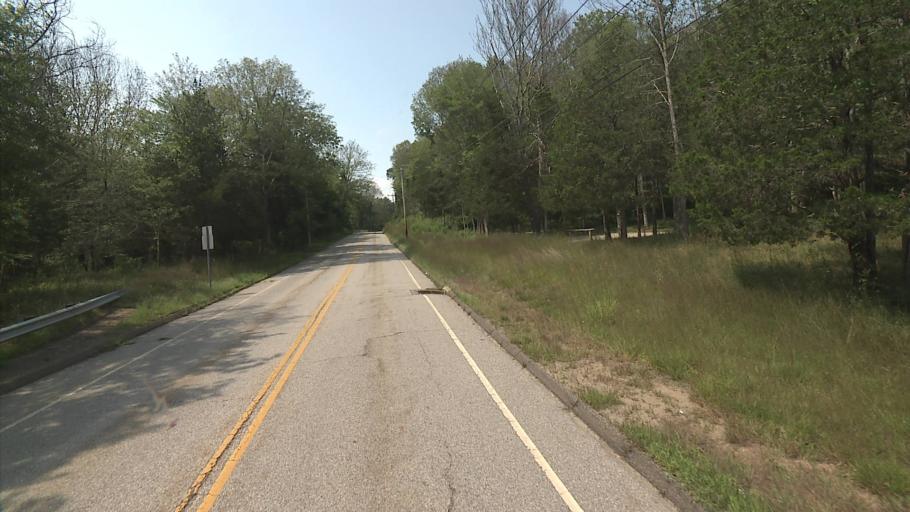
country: US
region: Connecticut
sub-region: Middlesex County
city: Deep River Center
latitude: 41.4237
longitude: -72.4023
